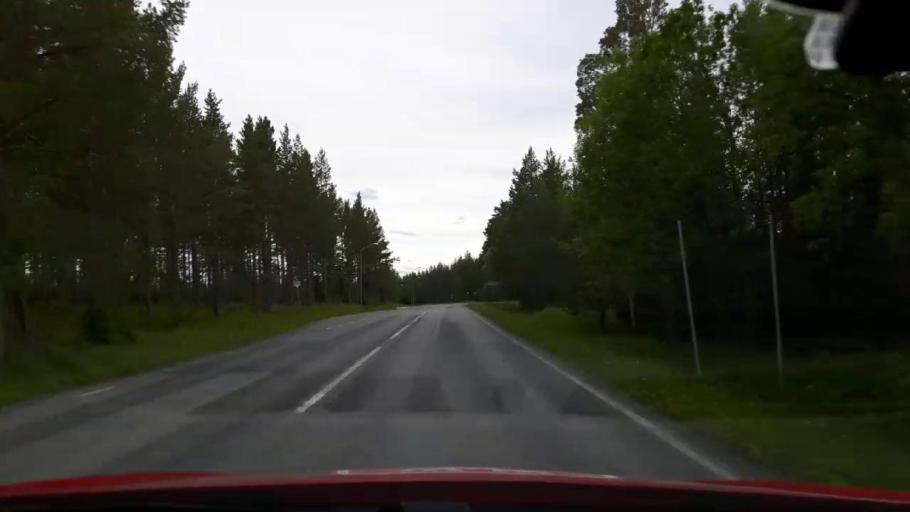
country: SE
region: Jaemtland
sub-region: Krokoms Kommun
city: Krokom
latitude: 63.1227
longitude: 14.4374
